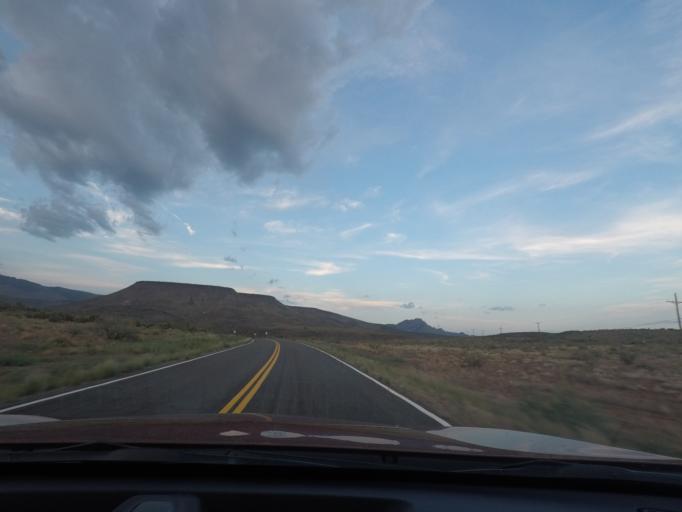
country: US
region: Arizona
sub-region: Yavapai County
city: Congress
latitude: 34.4744
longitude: -112.8274
